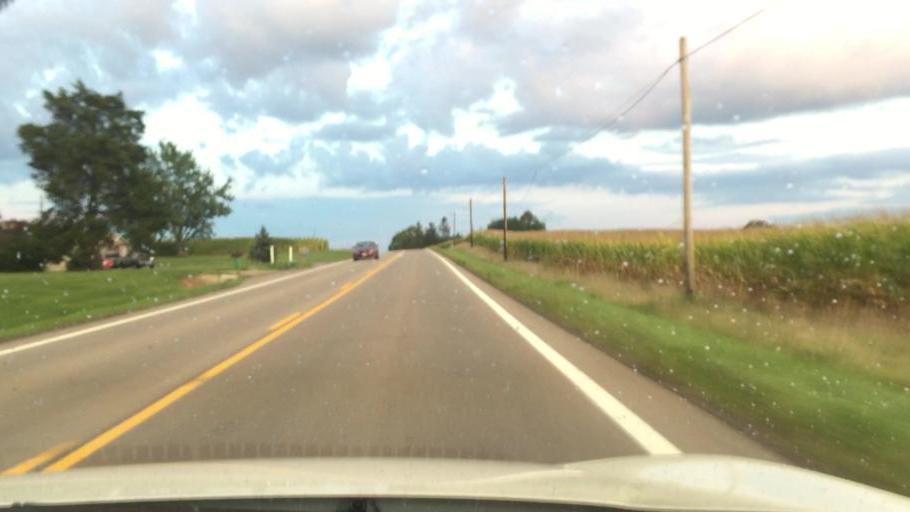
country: US
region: Ohio
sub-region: Champaign County
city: Mechanicsburg
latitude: 40.0636
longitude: -83.5452
